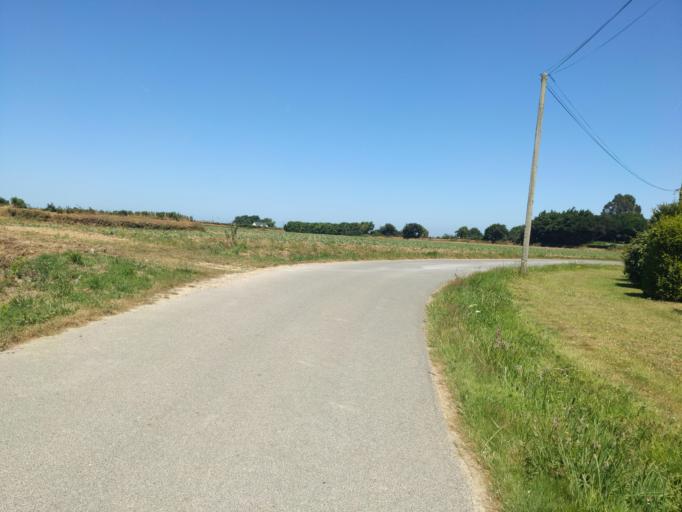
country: FR
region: Brittany
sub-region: Departement des Cotes-d'Armor
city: Plougrescant
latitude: 48.8198
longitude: -3.2112
